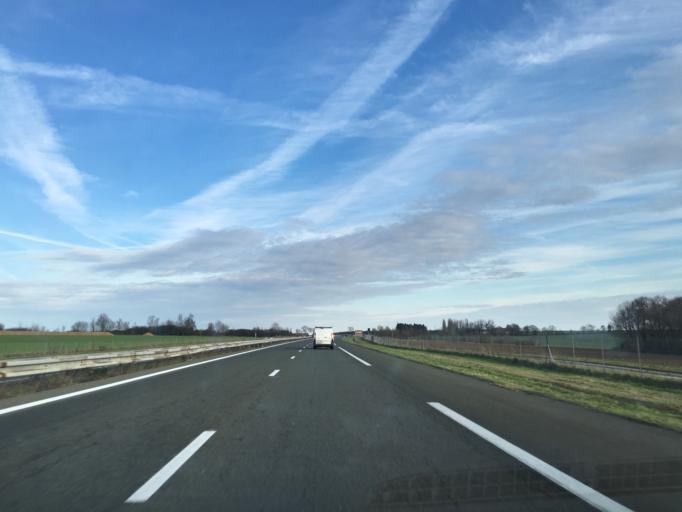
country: FR
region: Picardie
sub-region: Departement de l'Aisne
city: Essomes-sur-Marne
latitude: 49.0674
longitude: 3.3380
